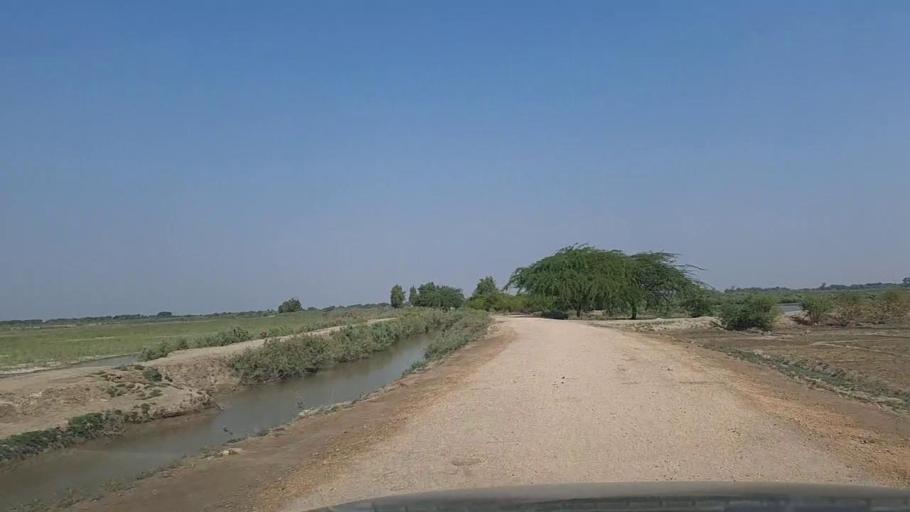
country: PK
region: Sindh
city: Mirpur Sakro
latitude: 24.5085
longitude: 67.7799
